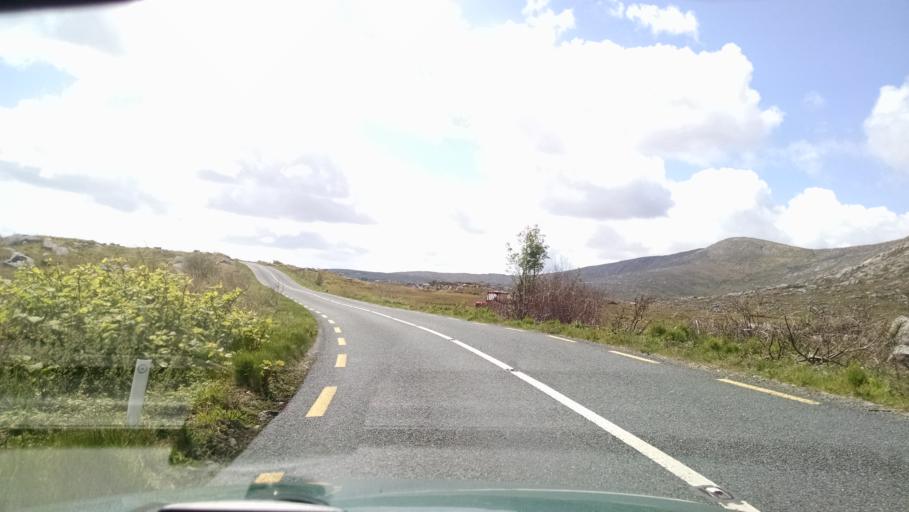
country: IE
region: Connaught
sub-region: County Galway
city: Oughterard
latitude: 53.3771
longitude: -9.6764
